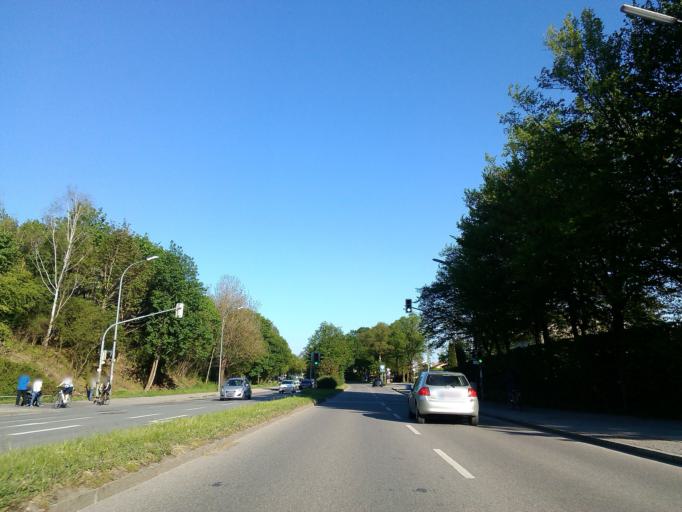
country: DE
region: Bavaria
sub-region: Upper Bavaria
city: Neuried
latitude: 48.0901
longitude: 11.4721
